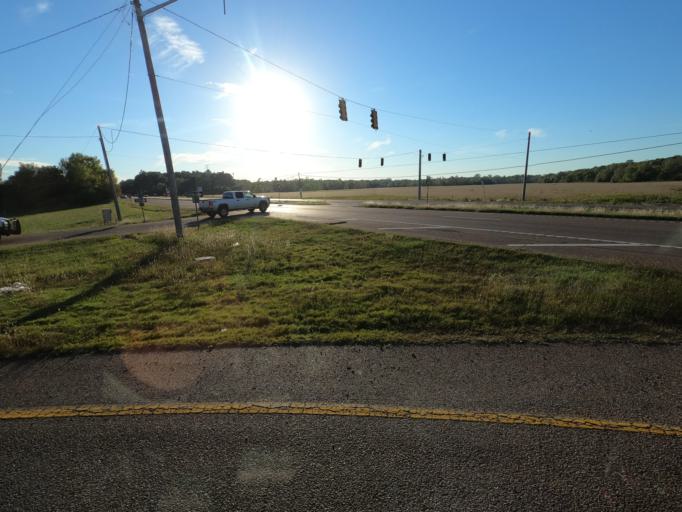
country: US
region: Tennessee
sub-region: Shelby County
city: Millington
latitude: 35.3323
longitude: -89.9195
